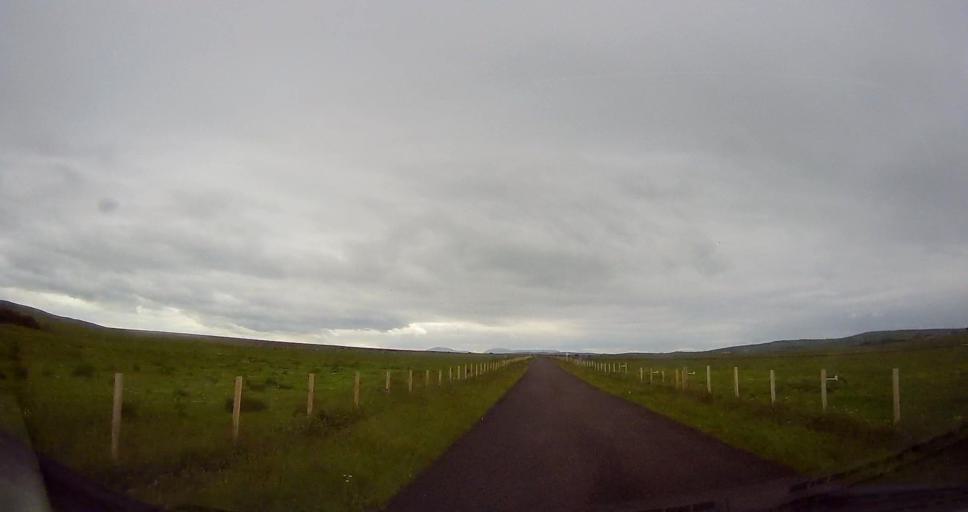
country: GB
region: Scotland
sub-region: Orkney Islands
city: Stromness
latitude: 59.1062
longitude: -3.2556
